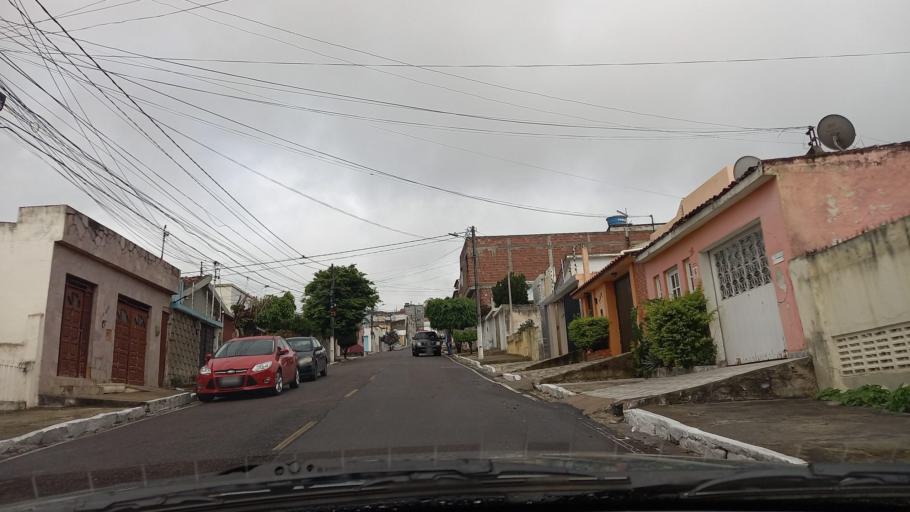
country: BR
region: Pernambuco
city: Garanhuns
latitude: -8.8955
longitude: -36.4926
